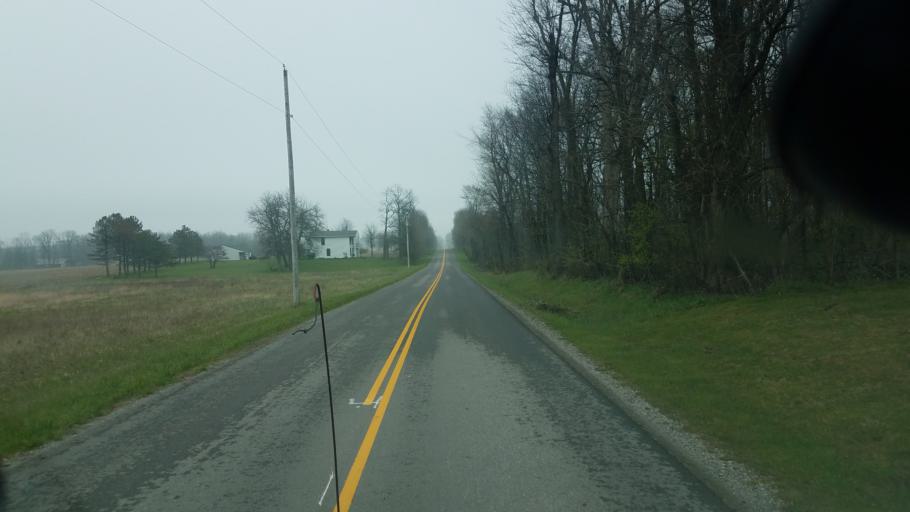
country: US
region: Ohio
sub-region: Logan County
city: Northwood
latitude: 40.4741
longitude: -83.7191
